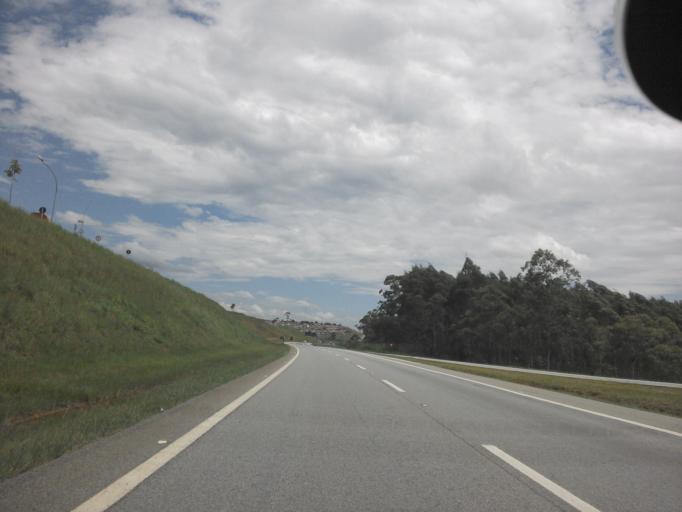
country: BR
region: Sao Paulo
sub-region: Cacapava
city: Cacapava
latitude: -23.1015
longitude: -45.6313
